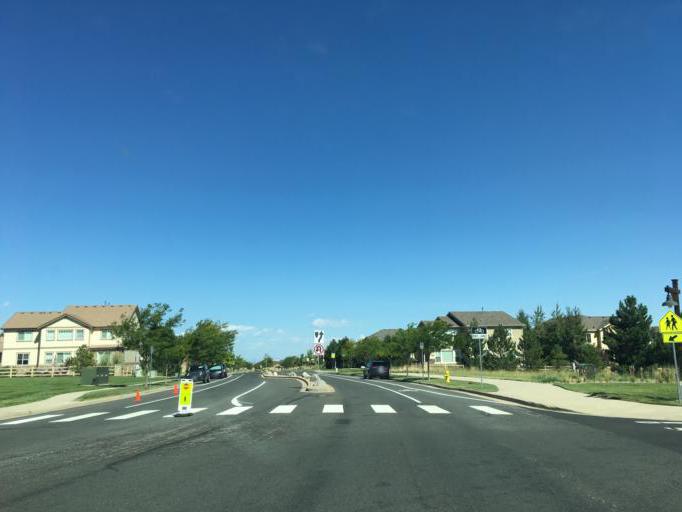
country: US
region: Colorado
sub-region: Douglas County
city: Parker
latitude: 39.5996
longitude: -104.6920
